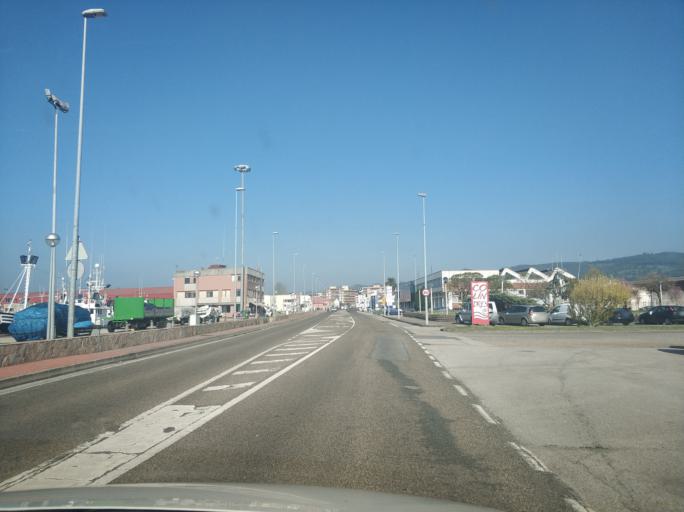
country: ES
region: Cantabria
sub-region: Provincia de Cantabria
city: Colindres
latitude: 43.3937
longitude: -3.4629
